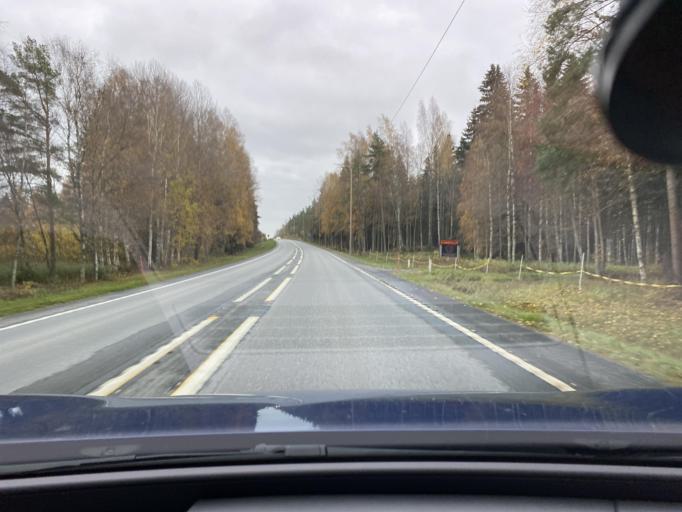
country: FI
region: Varsinais-Suomi
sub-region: Vakka-Suomi
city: Laitila
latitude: 60.9337
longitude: 21.6061
